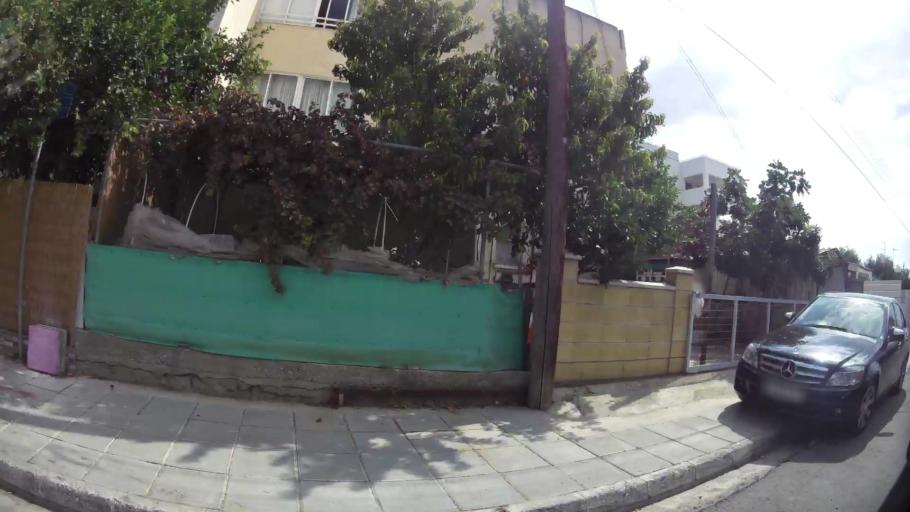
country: CY
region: Lefkosia
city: Geri
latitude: 35.1126
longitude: 33.3744
